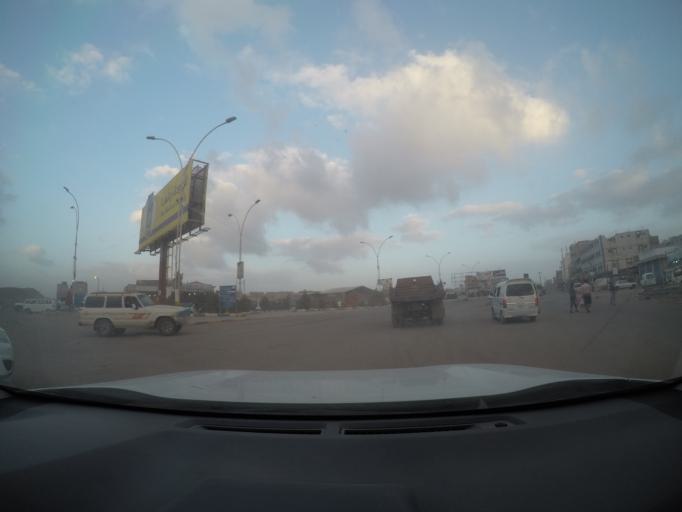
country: YE
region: Aden
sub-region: Ash Shaikh Outhman
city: Ash Shaykh `Uthman
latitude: 12.8989
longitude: 44.9829
